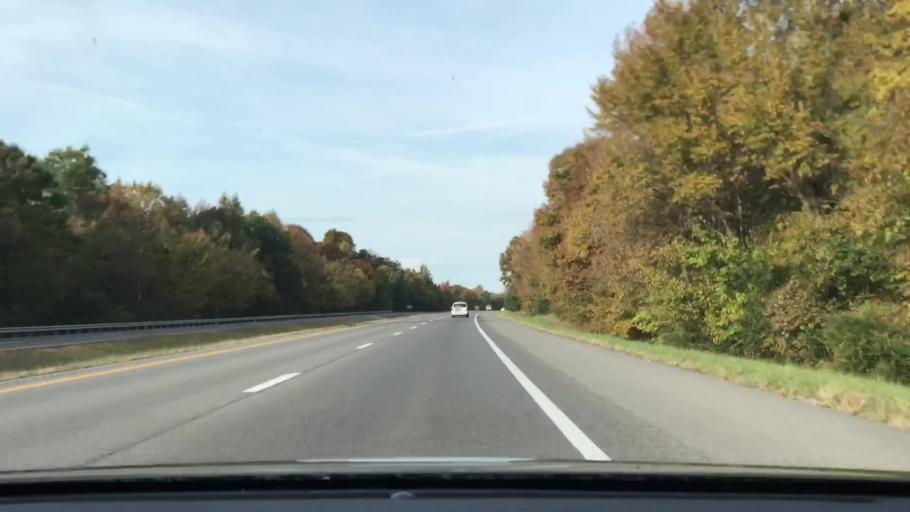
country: US
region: Kentucky
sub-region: Graves County
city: Mayfield
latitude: 36.7704
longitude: -88.6124
